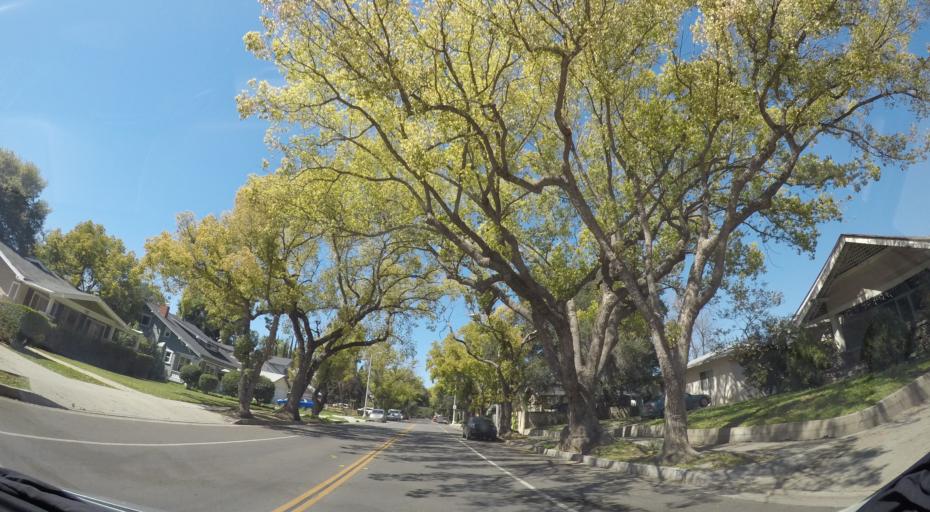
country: US
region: California
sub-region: Los Angeles County
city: Pasadena
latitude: 34.1571
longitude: -118.1559
